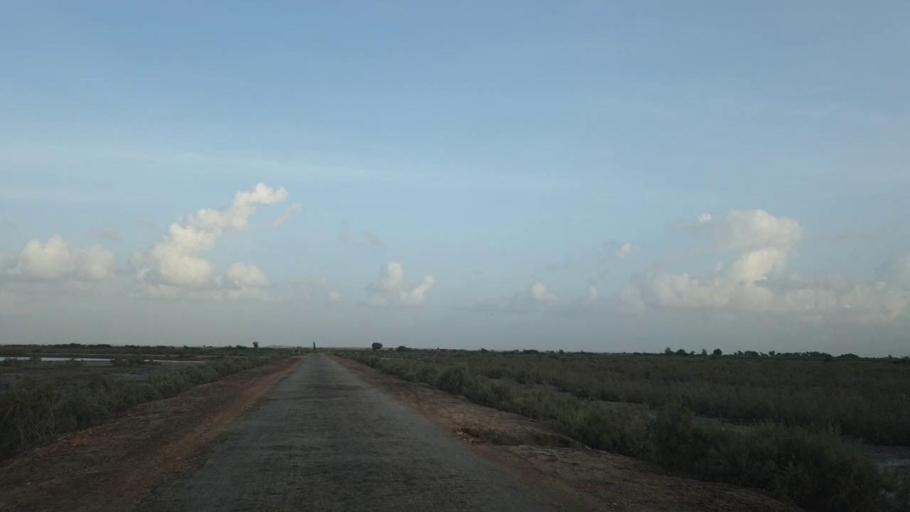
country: PK
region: Sindh
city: Kadhan
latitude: 24.5660
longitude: 69.1201
